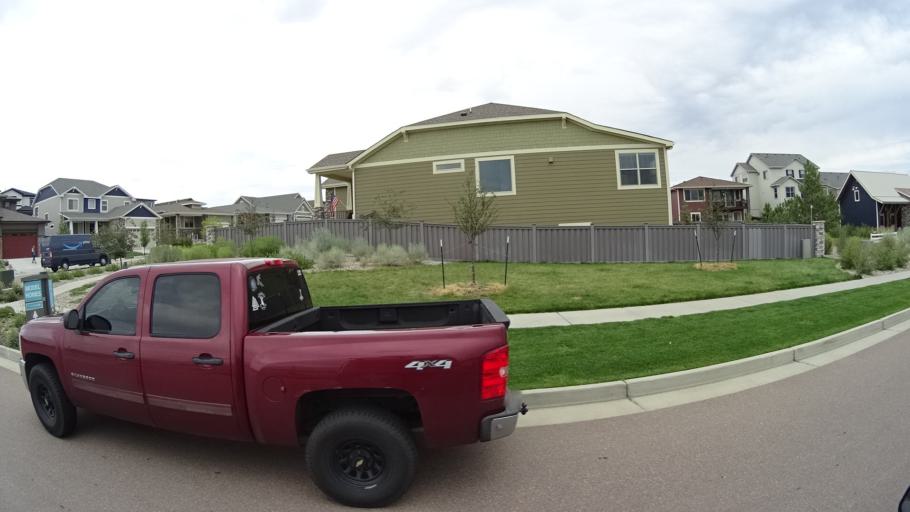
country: US
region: Colorado
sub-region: El Paso County
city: Gleneagle
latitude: 39.0014
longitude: -104.8054
